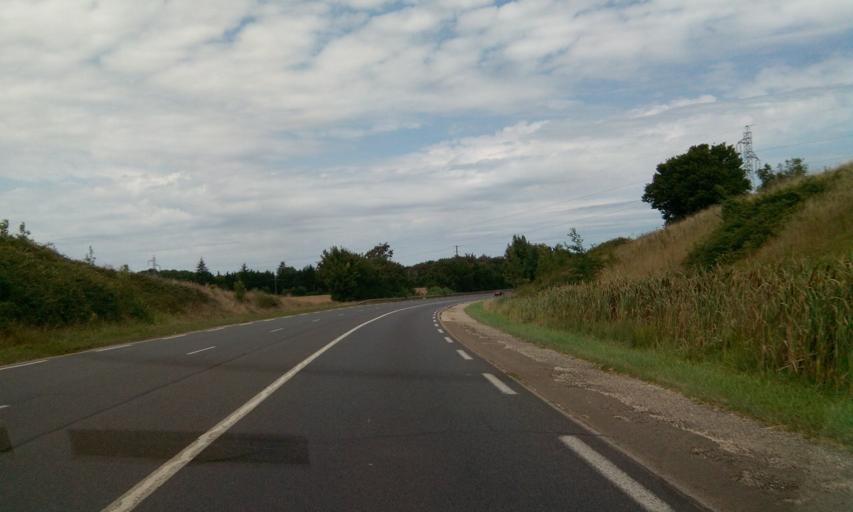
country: FR
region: Poitou-Charentes
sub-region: Departement des Deux-Sevres
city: Melle
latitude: 46.2117
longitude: -0.1549
